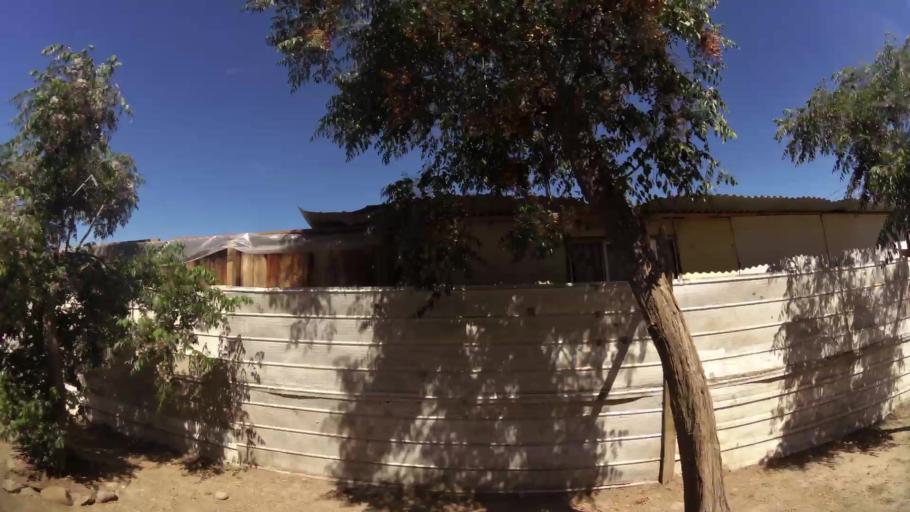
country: CL
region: Santiago Metropolitan
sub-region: Provincia de Maipo
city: San Bernardo
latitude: -33.5806
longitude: -70.6852
